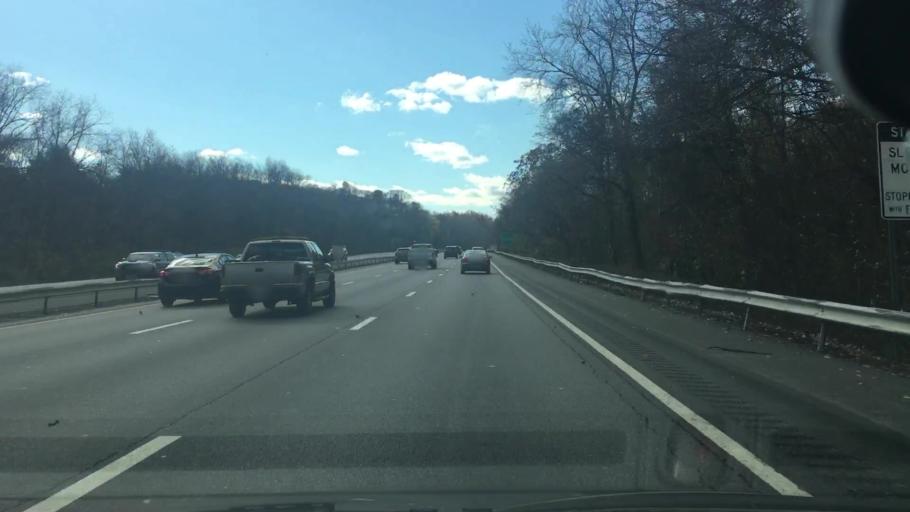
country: US
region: New York
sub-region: Westchester County
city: Goldens Bridge
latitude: 41.2793
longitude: -73.6819
